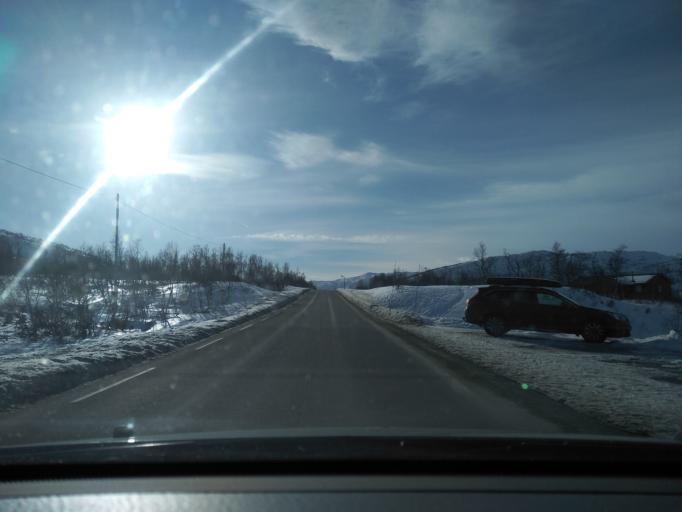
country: NO
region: Aust-Agder
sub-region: Bykle
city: Hovden
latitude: 59.6480
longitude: 7.4689
